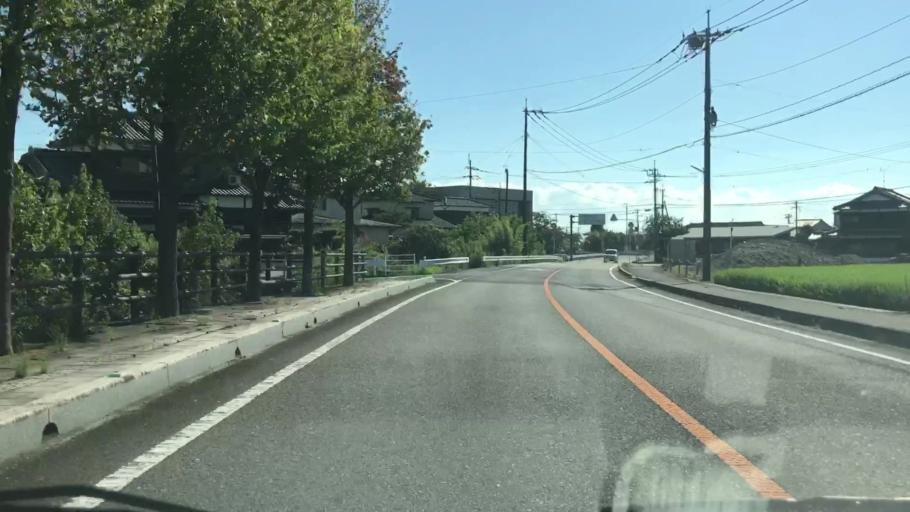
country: JP
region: Saga Prefecture
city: Okawa
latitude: 33.2259
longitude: 130.3537
